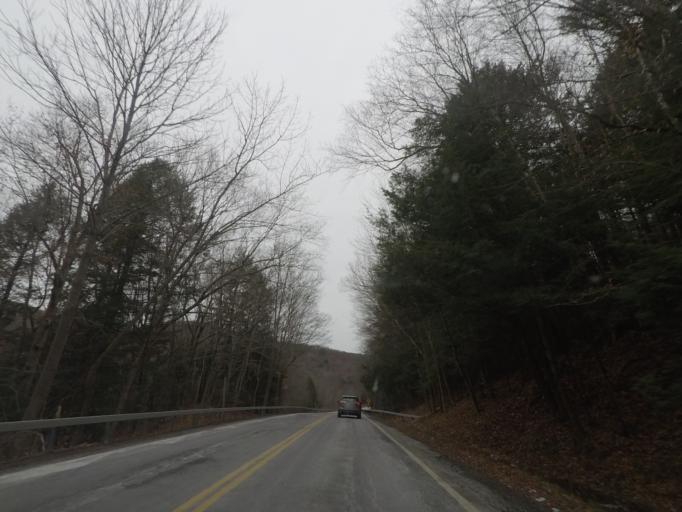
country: US
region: Massachusetts
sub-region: Berkshire County
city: Williamstown
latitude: 42.7481
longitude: -73.3324
